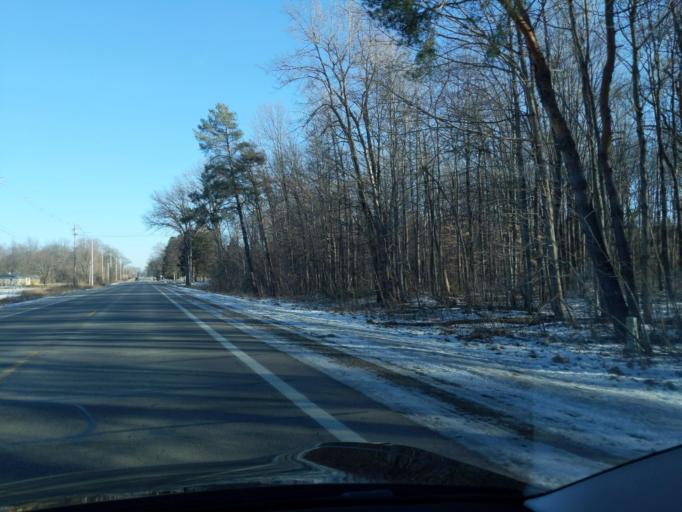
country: US
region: Michigan
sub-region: Ingham County
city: Stockbridge
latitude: 42.3937
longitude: -84.2817
